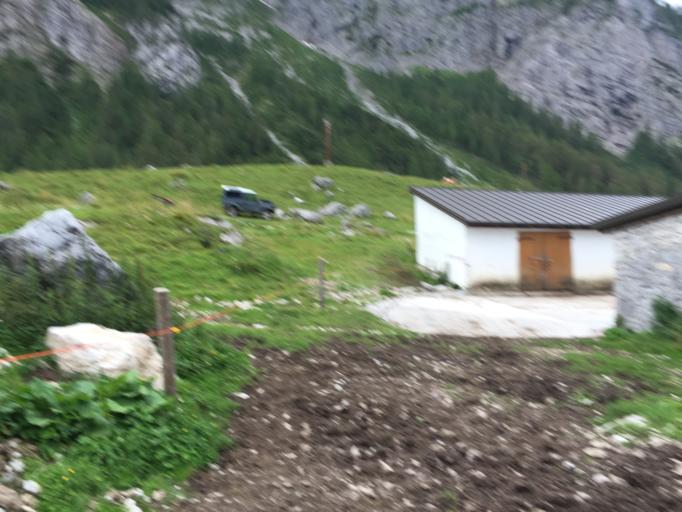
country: IT
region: Friuli Venezia Giulia
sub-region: Provincia di Udine
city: Forni Avoltri
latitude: 46.5623
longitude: 12.7646
